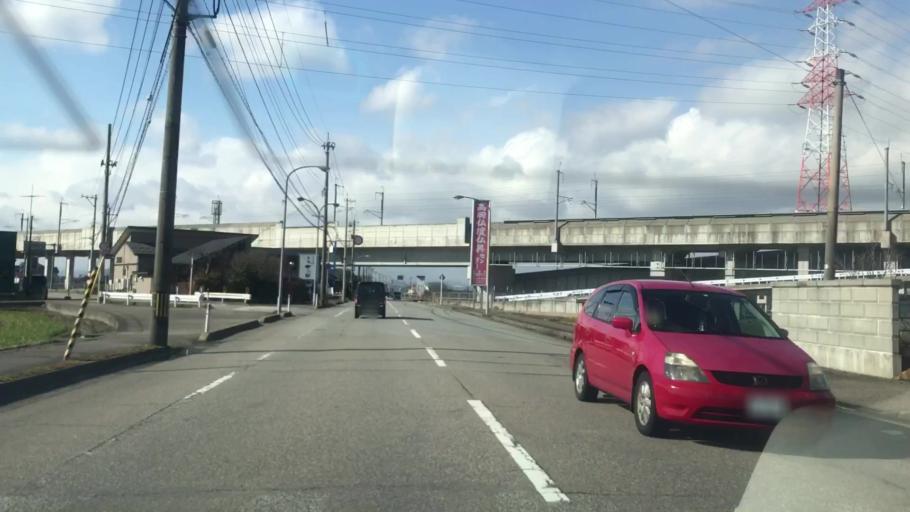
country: JP
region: Toyama
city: Nishishinminato
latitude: 36.7221
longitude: 137.0721
